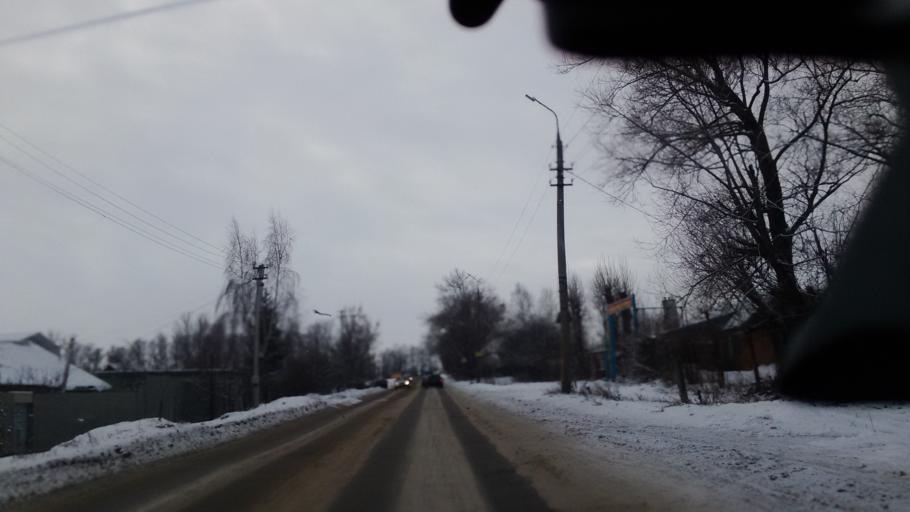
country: RU
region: Tula
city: Bogoroditsk
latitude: 53.7652
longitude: 38.1093
